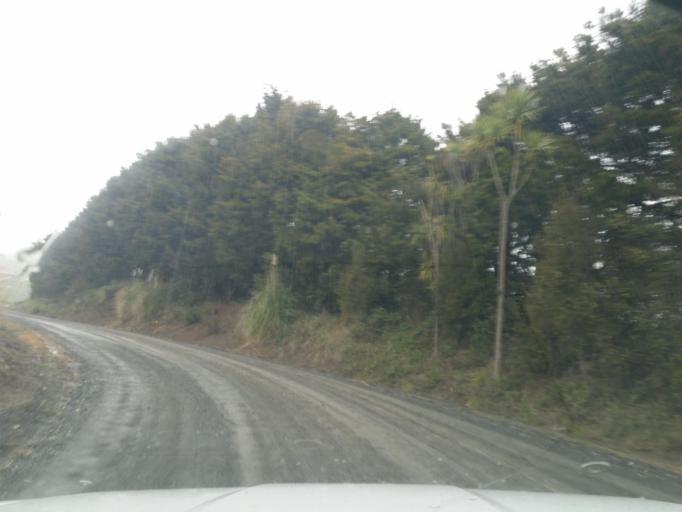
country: NZ
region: Northland
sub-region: Whangarei
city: Maungatapere
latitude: -36.0425
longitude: 174.1734
